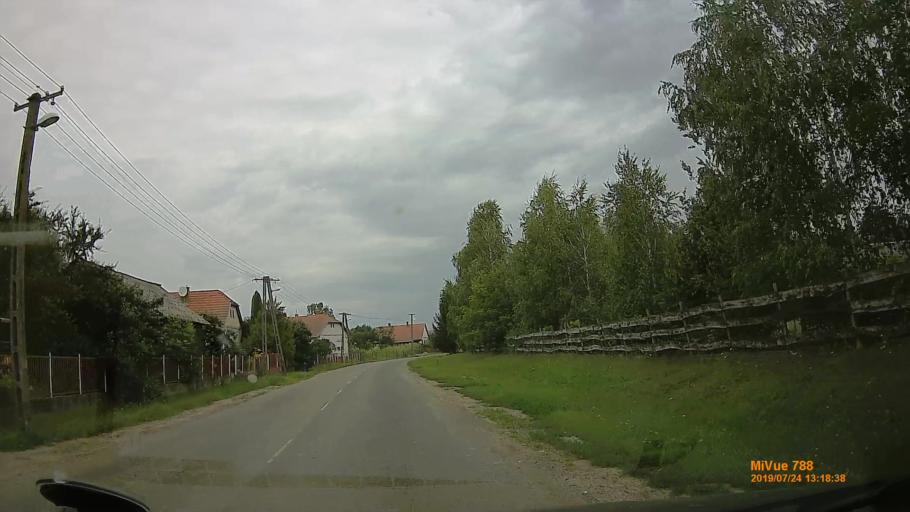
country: HU
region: Szabolcs-Szatmar-Bereg
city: Vasarosnameny
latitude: 48.1921
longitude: 22.4044
